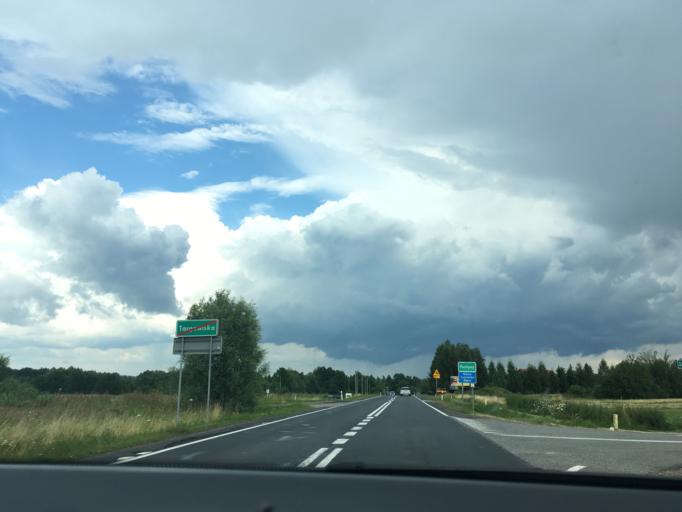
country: PL
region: Subcarpathian Voivodeship
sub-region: Powiat krosnienski
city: Kroscienko Wyzne
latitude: 49.6542
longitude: 21.8264
